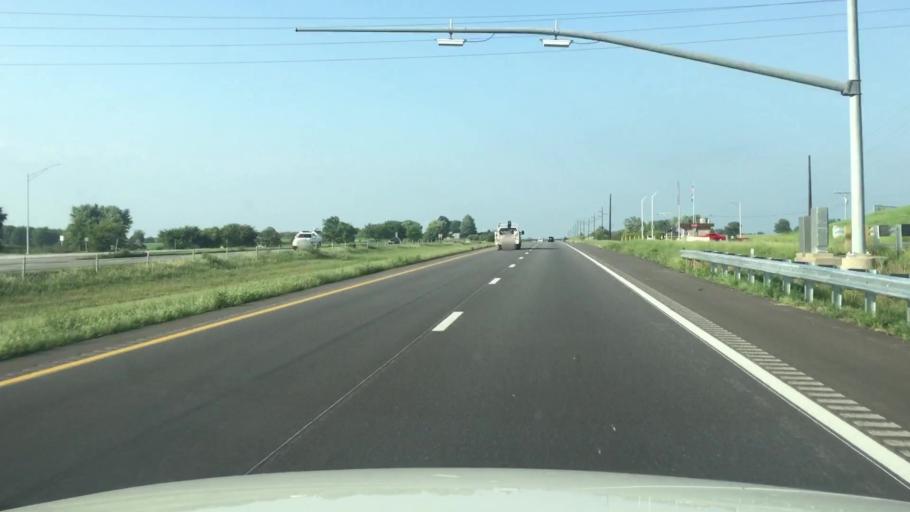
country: US
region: Missouri
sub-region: Clay County
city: Kearney
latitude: 39.3159
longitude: -94.4000
